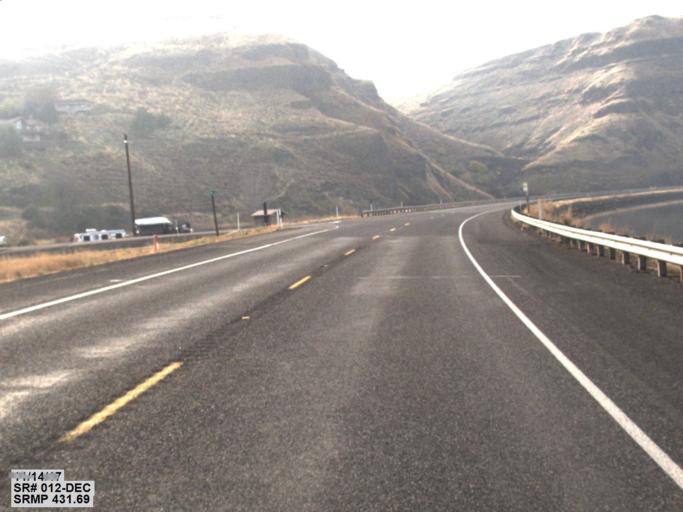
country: US
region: Washington
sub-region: Asotin County
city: West Clarkston-Highland
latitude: 46.4157
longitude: -117.0864
